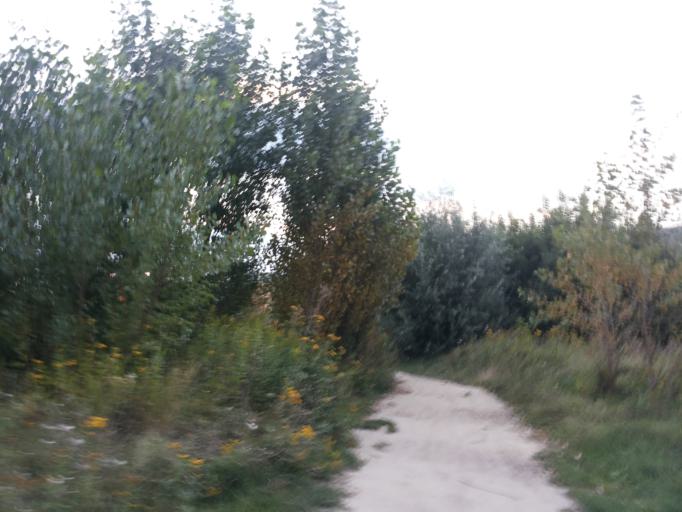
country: PL
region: Masovian Voivodeship
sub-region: Warszawa
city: Targowek
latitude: 52.3252
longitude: 21.0503
